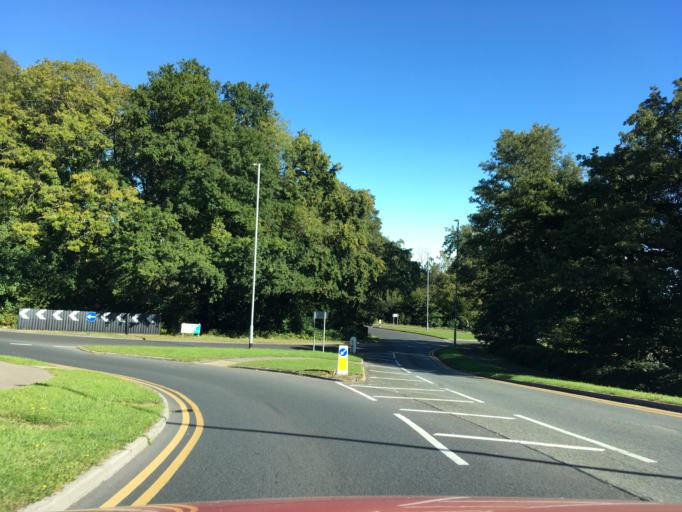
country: GB
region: Wales
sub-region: Torfaen County Borough
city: Cwmbran
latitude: 51.6427
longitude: -3.0506
